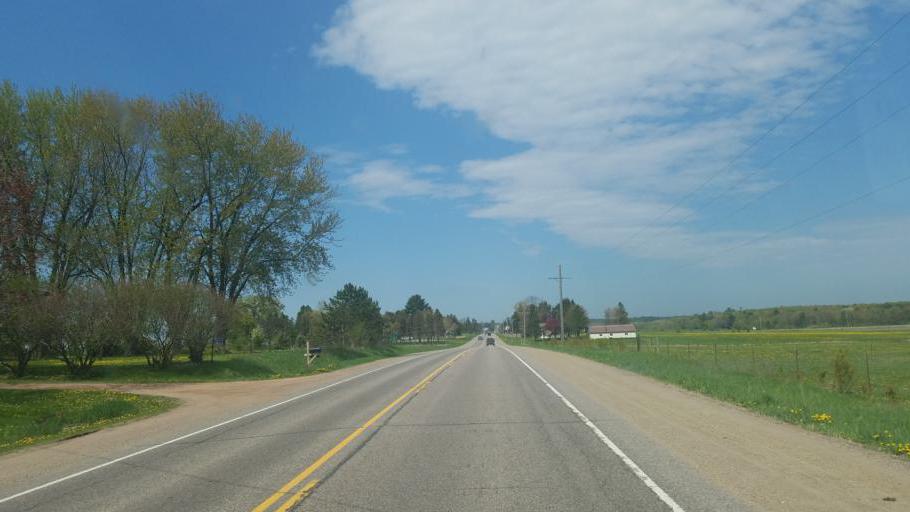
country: US
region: Wisconsin
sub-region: Clark County
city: Loyal
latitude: 44.5829
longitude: -90.3834
